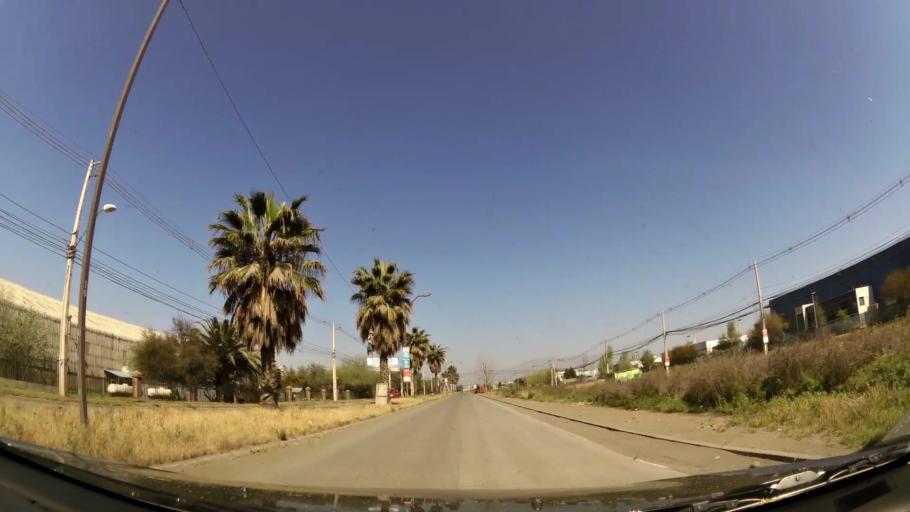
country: CL
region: Santiago Metropolitan
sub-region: Provincia de Chacabuco
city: Chicureo Abajo
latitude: -33.3160
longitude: -70.7290
